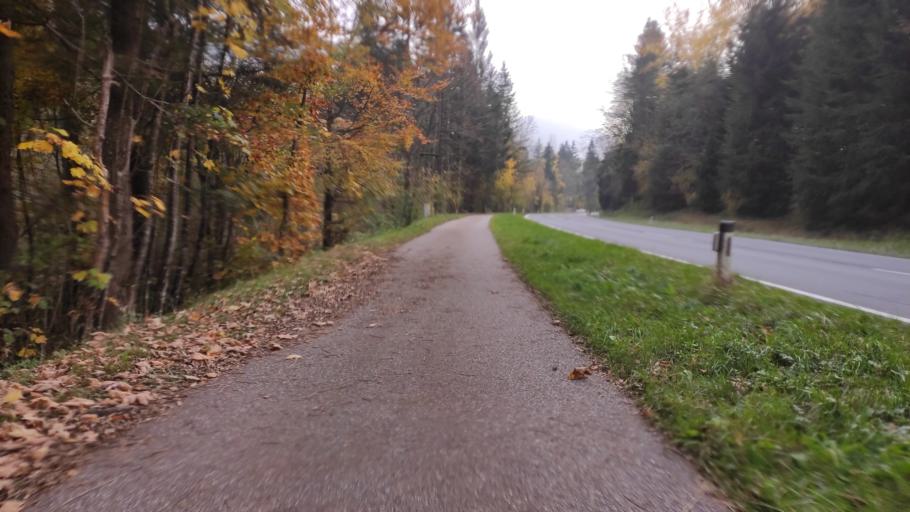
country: AT
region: Salzburg
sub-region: Politischer Bezirk Salzburg-Umgebung
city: Ebenau
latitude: 47.7718
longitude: 13.1820
